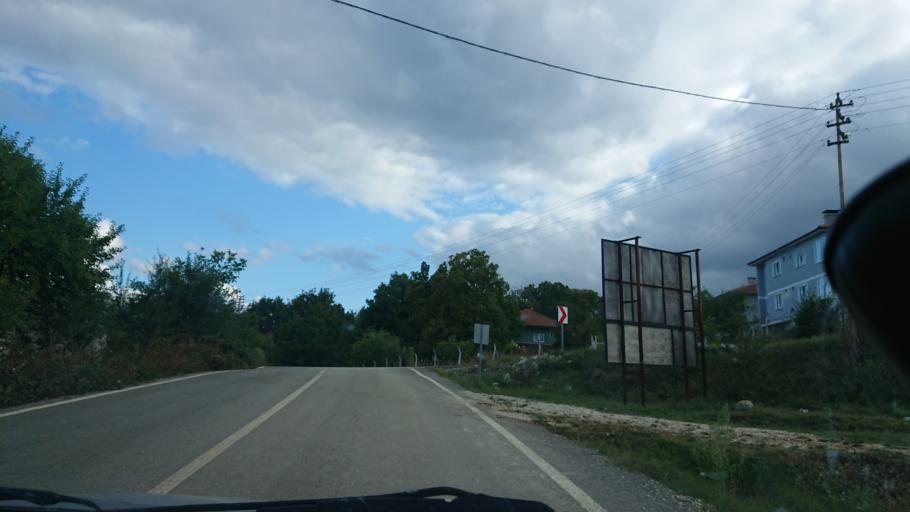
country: TR
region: Bilecik
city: Pazaryeri
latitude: 40.0110
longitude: 29.7983
